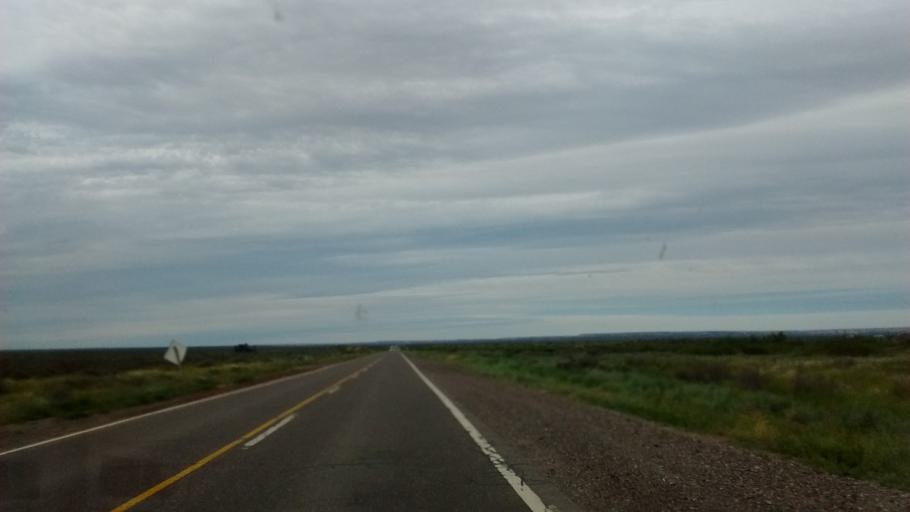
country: AR
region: Rio Negro
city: Catriel
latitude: -38.0342
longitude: -67.9170
